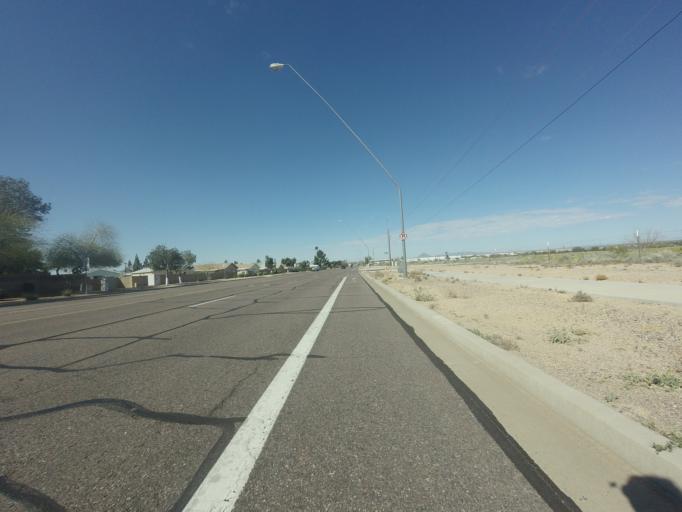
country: US
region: Arizona
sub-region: Maricopa County
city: Mesa
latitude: 33.4664
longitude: -111.7053
